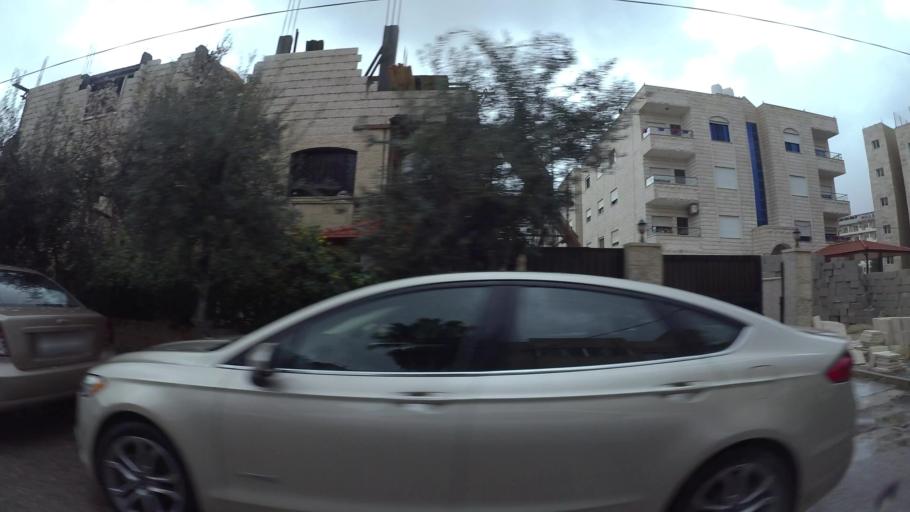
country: JO
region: Amman
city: Al Jubayhah
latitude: 32.0318
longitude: 35.8756
